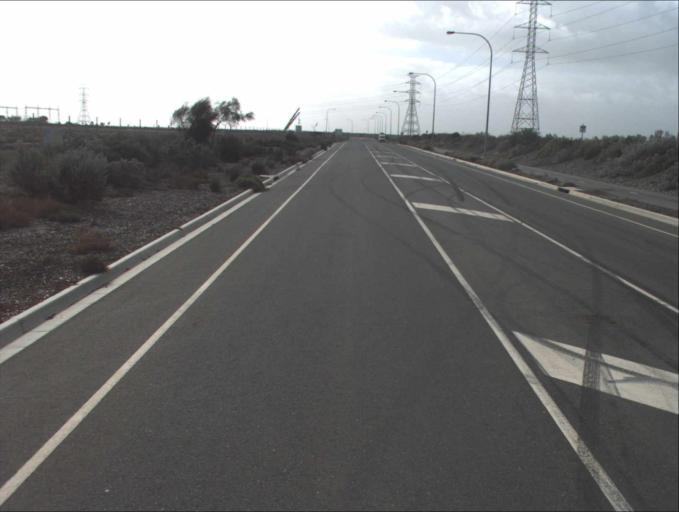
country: AU
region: South Australia
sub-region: Port Adelaide Enfield
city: Birkenhead
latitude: -34.7742
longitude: 138.5091
